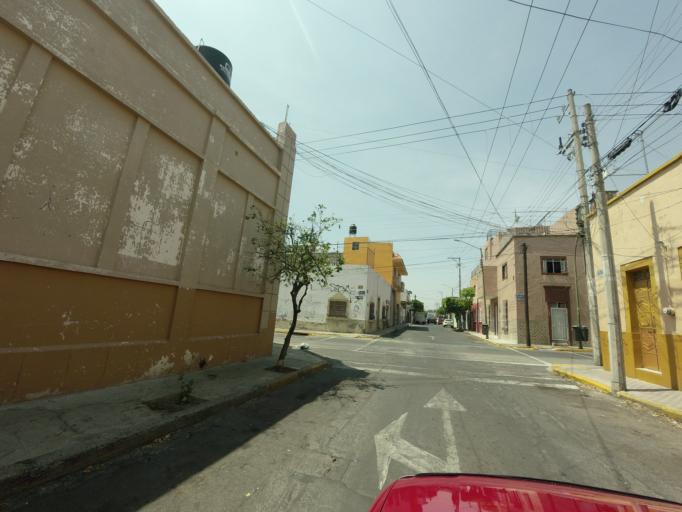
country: MX
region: Jalisco
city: Guadalajara
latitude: 20.6860
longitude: -103.3410
